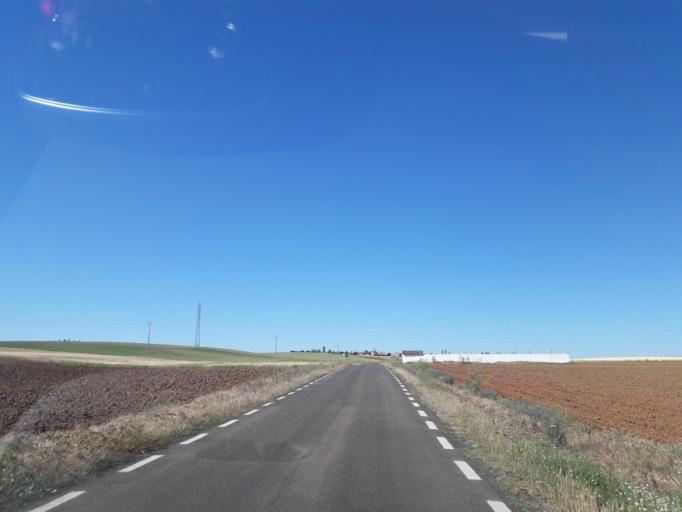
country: ES
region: Castille and Leon
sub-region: Provincia de Salamanca
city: Parada de Arriba
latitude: 40.9954
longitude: -5.7884
